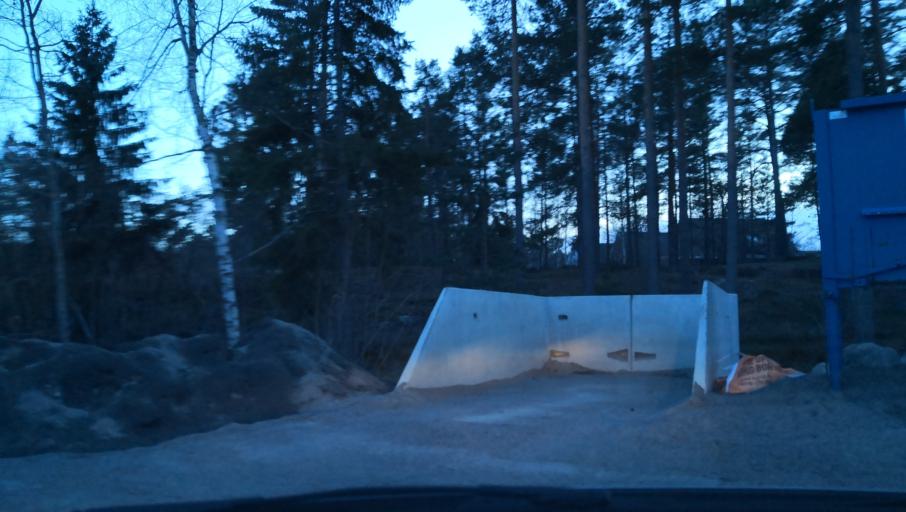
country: SE
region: Stockholm
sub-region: Varmdo Kommun
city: Gustavsberg
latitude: 59.3390
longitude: 18.3857
